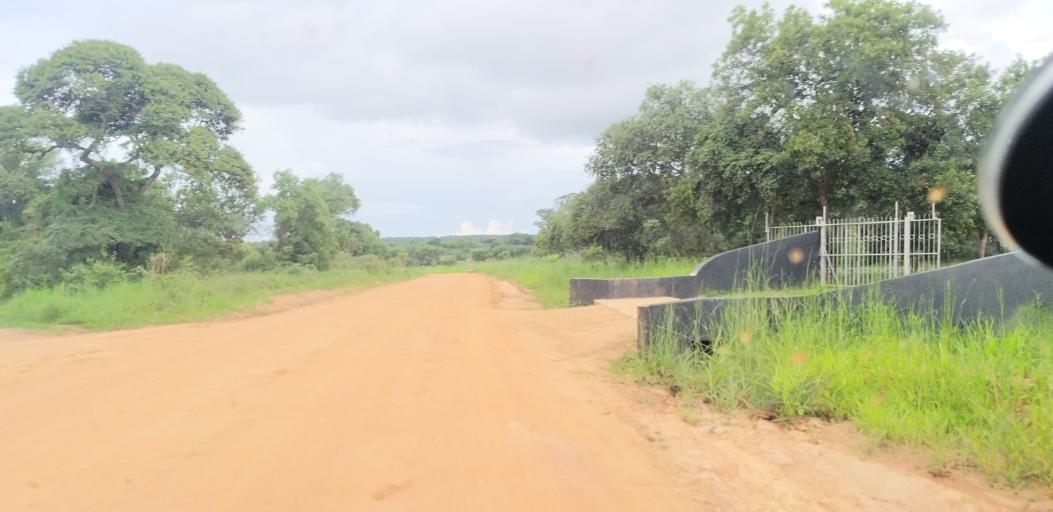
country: ZM
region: Lusaka
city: Lusaka
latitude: -15.1977
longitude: 28.4415
